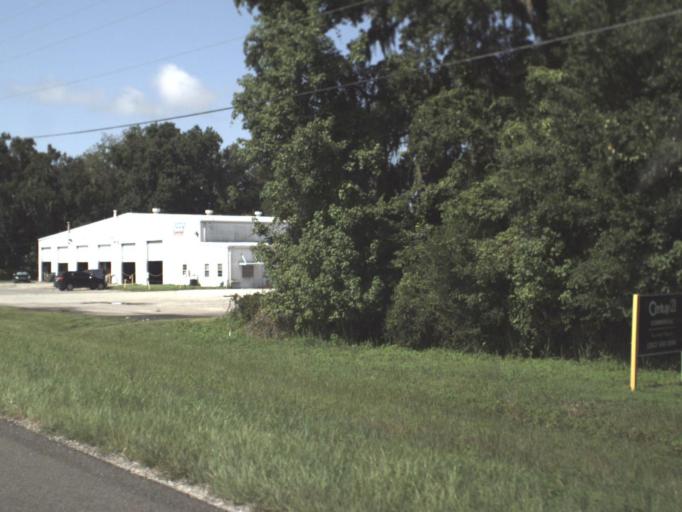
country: US
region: Florida
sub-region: Hernando County
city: South Brooksville
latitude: 28.5498
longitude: -82.4209
